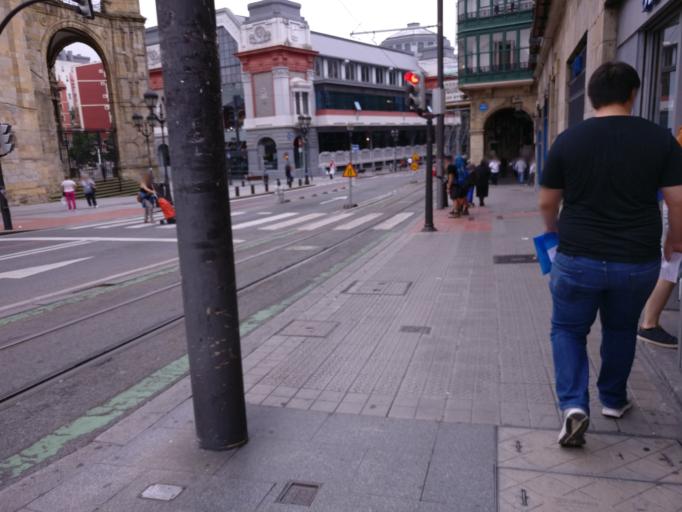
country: ES
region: Basque Country
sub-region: Bizkaia
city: Santutxu
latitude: 43.2555
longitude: -2.9229
